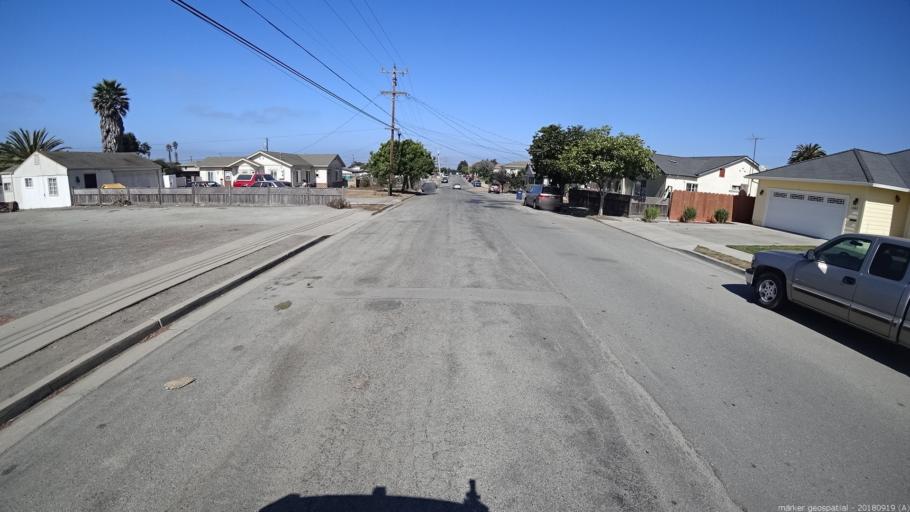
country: US
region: California
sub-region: Monterey County
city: Castroville
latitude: 36.7689
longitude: -121.7552
